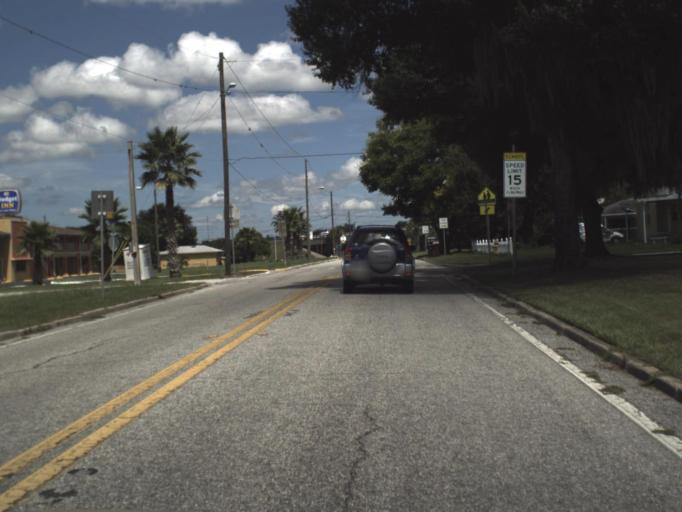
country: US
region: Florida
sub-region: Polk County
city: Lake Wales
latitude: 27.8918
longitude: -81.5814
